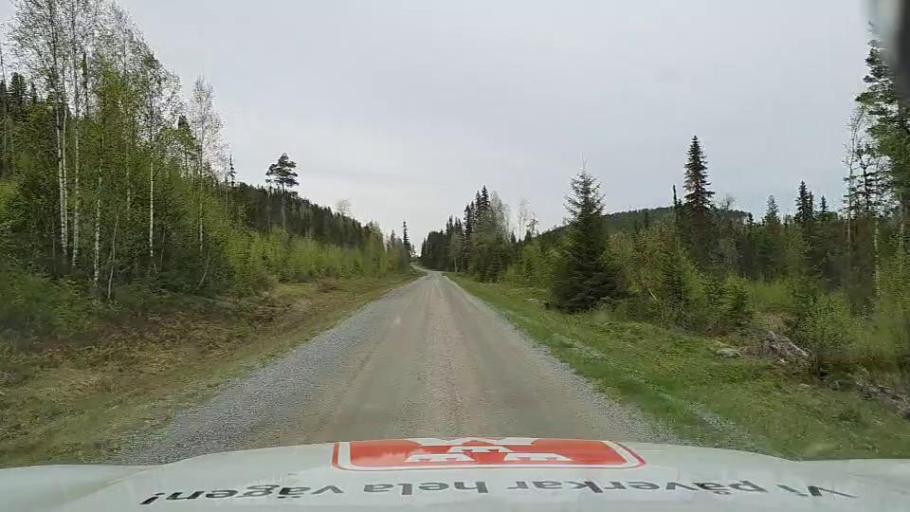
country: SE
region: Jaemtland
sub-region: Bergs Kommun
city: Hoverberg
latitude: 62.5392
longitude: 14.7007
